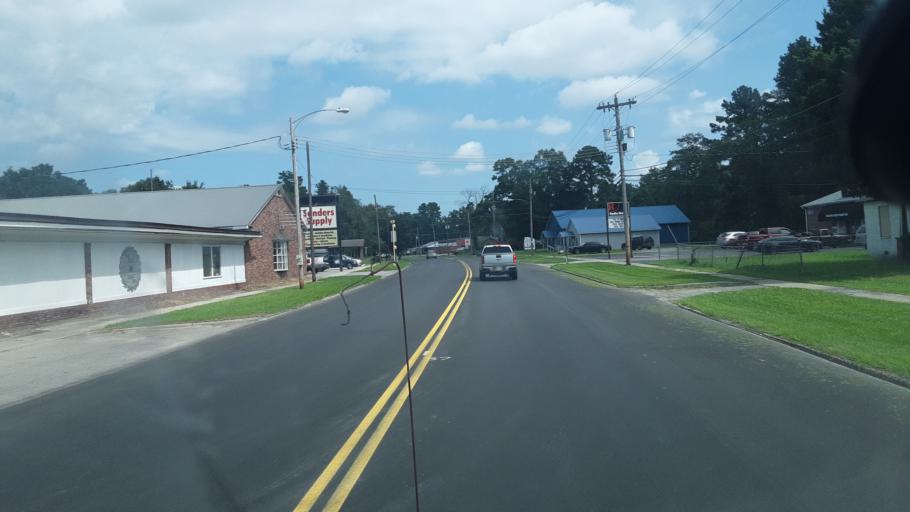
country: US
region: South Carolina
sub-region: Bamberg County
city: Bamberg
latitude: 33.3019
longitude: -81.0337
